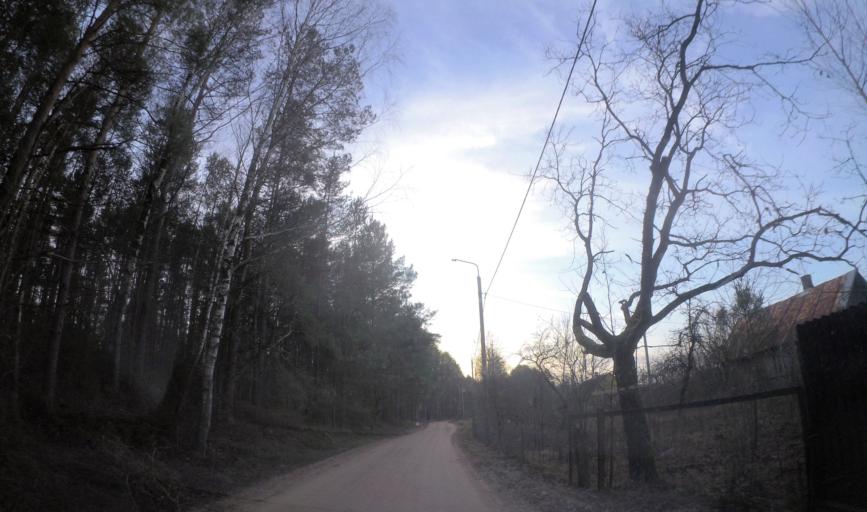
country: LT
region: Alytaus apskritis
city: Druskininkai
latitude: 53.9155
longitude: 24.1885
